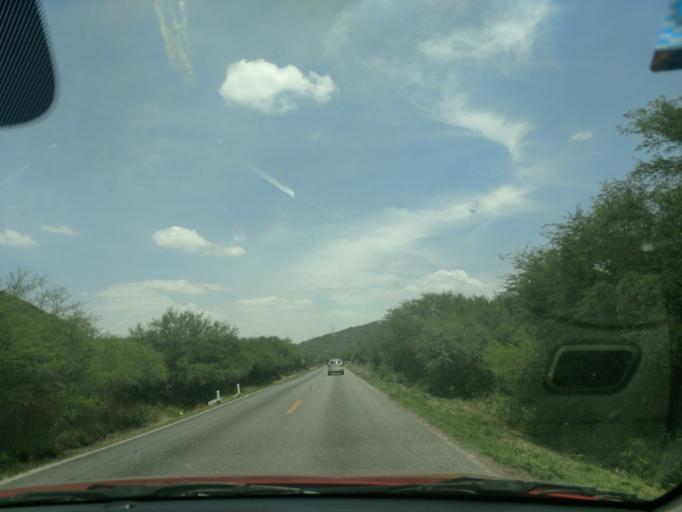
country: MX
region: San Luis Potosi
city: Ciudad Fernandez
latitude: 21.9996
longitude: -100.1416
